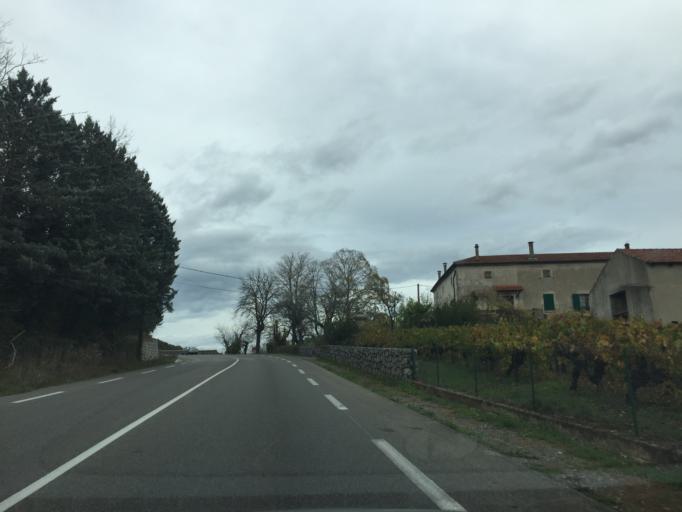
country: FR
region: Rhone-Alpes
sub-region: Departement de l'Ardeche
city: Largentiere
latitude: 44.5088
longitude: 4.3164
